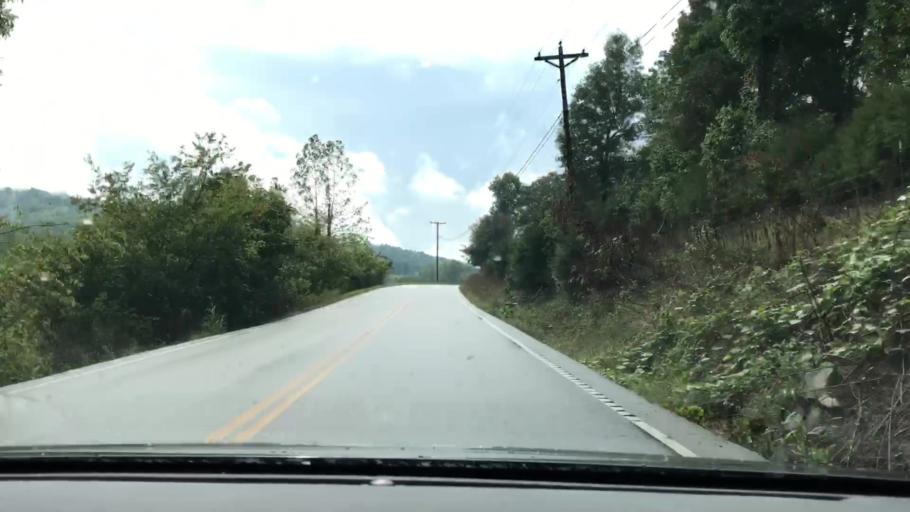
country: US
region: Tennessee
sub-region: Smith County
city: Carthage
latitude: 36.3673
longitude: -85.9521
